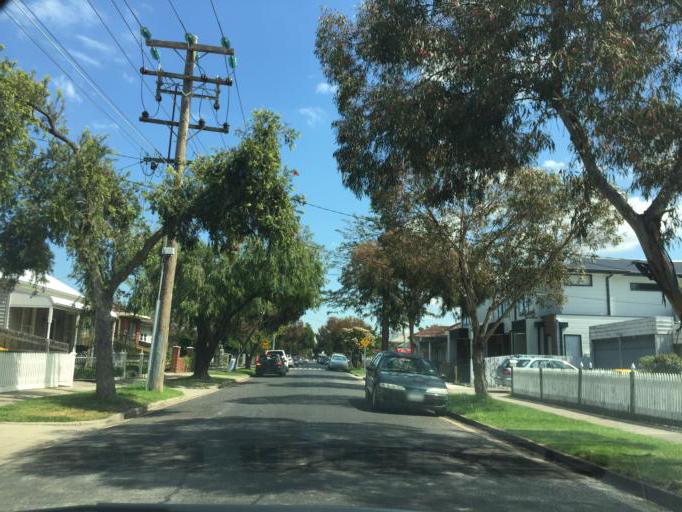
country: AU
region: Victoria
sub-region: Maribyrnong
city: West Footscray
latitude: -37.7911
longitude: 144.8784
